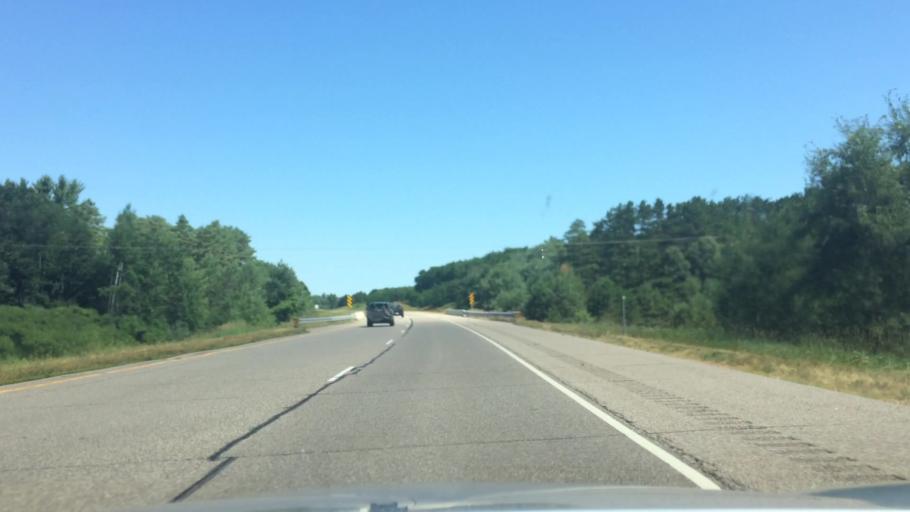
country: US
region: Wisconsin
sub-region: Marquette County
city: Westfield
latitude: 44.0817
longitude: -89.5323
